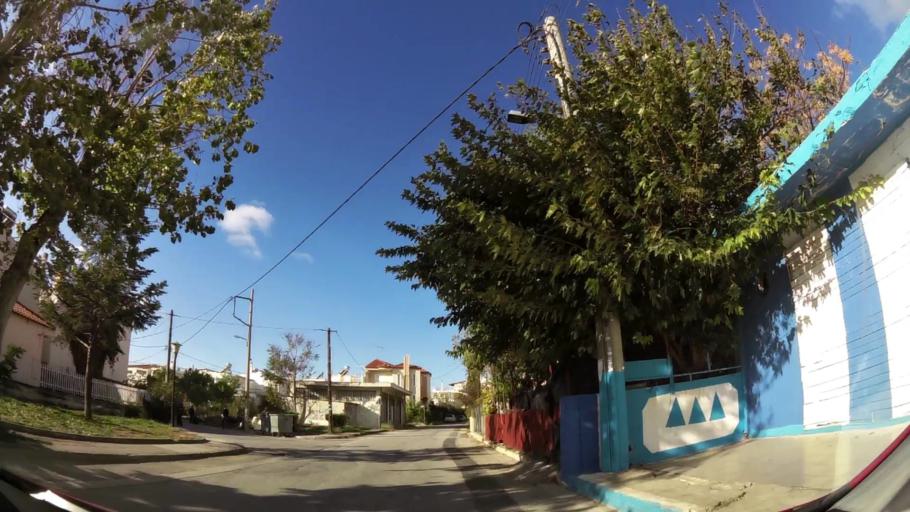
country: GR
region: Attica
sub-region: Nomarchia Anatolikis Attikis
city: Acharnes
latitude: 38.0705
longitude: 23.7433
